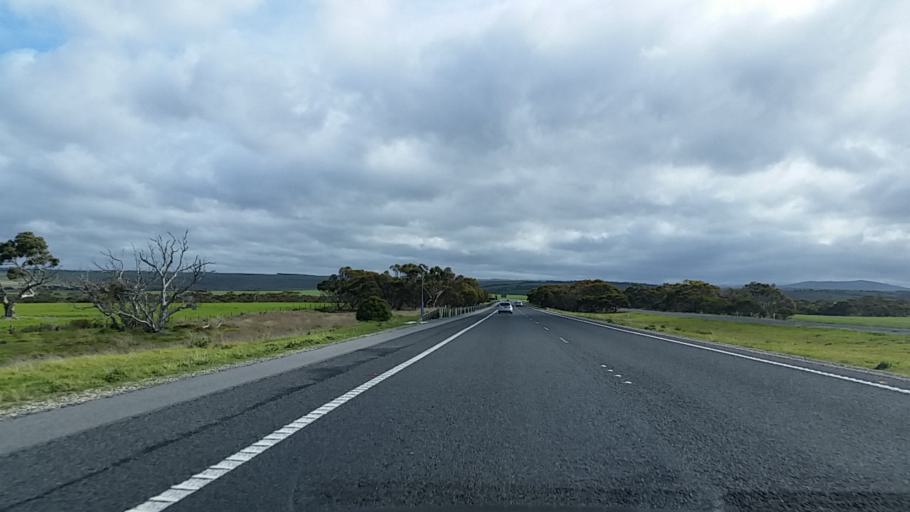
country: AU
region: South Australia
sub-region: Mount Barker
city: Callington
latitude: -35.1315
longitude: 139.0539
